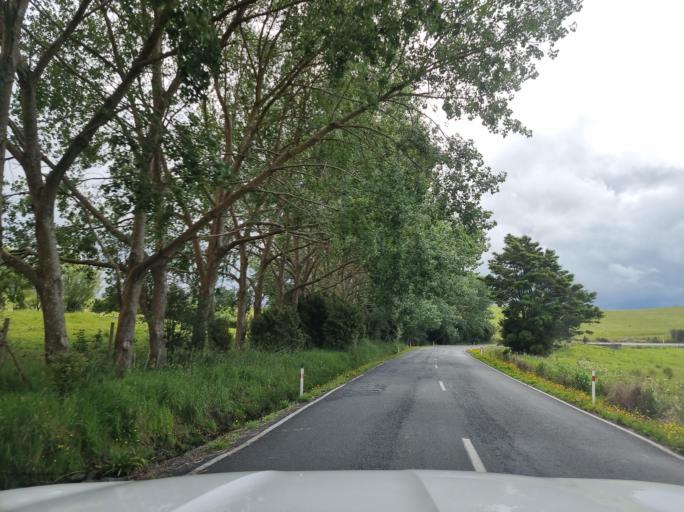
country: NZ
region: Northland
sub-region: Whangarei
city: Maungatapere
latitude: -35.9198
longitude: 174.2663
